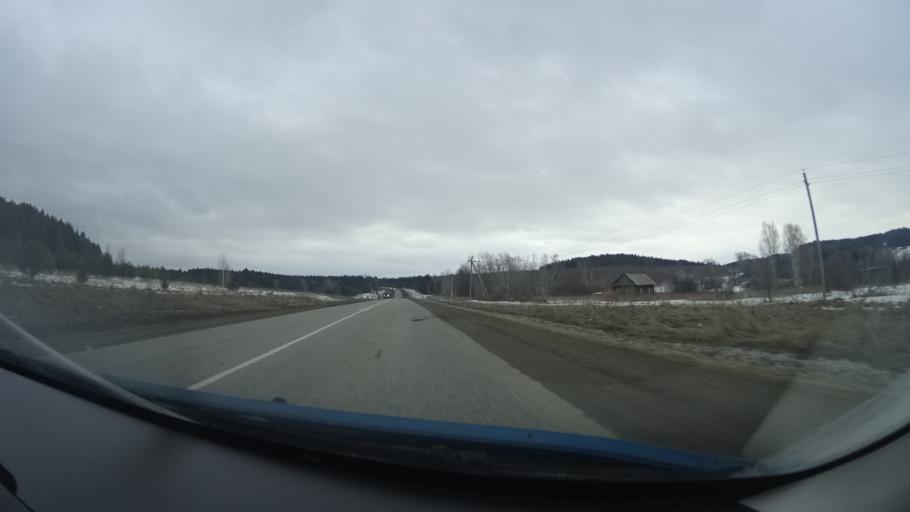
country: RU
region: Perm
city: Osa
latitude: 57.3290
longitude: 55.5904
